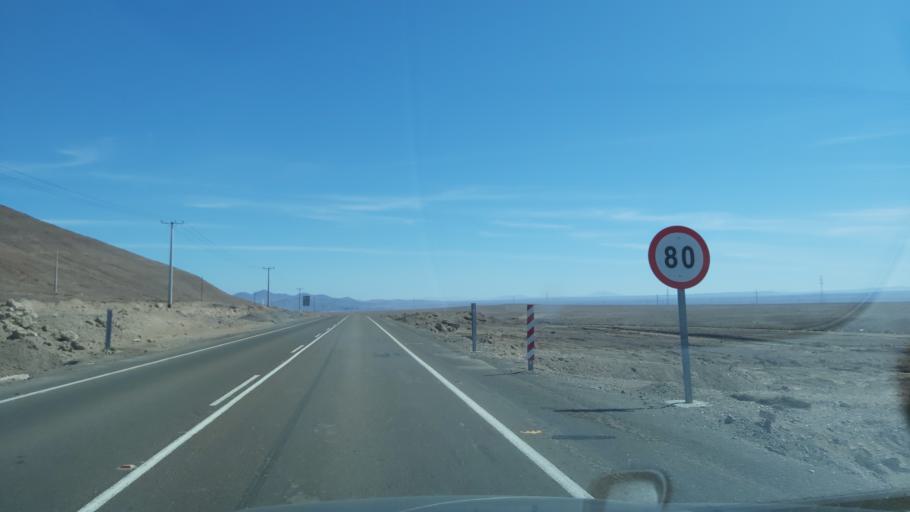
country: CL
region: Atacama
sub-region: Provincia de Chanaral
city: Diego de Almagro
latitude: -26.4596
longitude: -69.9854
